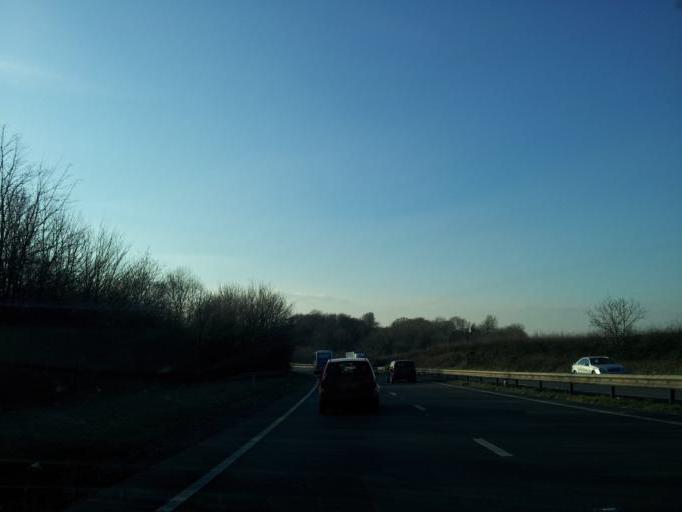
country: GB
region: England
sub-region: Devon
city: Okehampton
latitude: 50.7367
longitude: -3.8965
